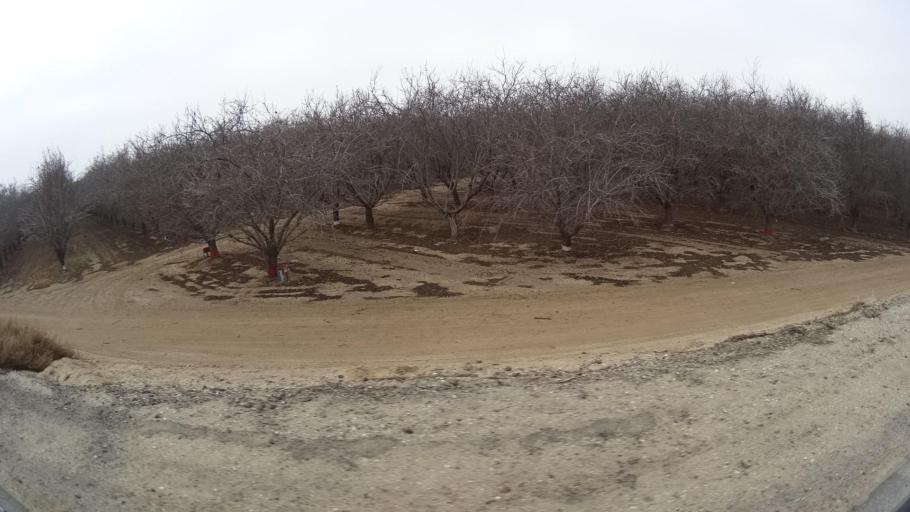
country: US
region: California
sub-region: Kern County
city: Maricopa
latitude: 35.1053
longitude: -119.3430
